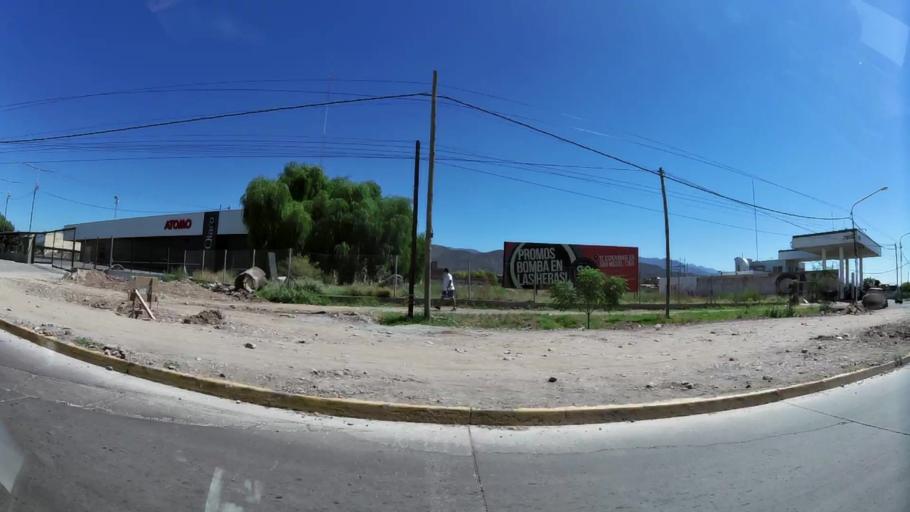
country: AR
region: Mendoza
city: Las Heras
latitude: -32.8518
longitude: -68.8599
